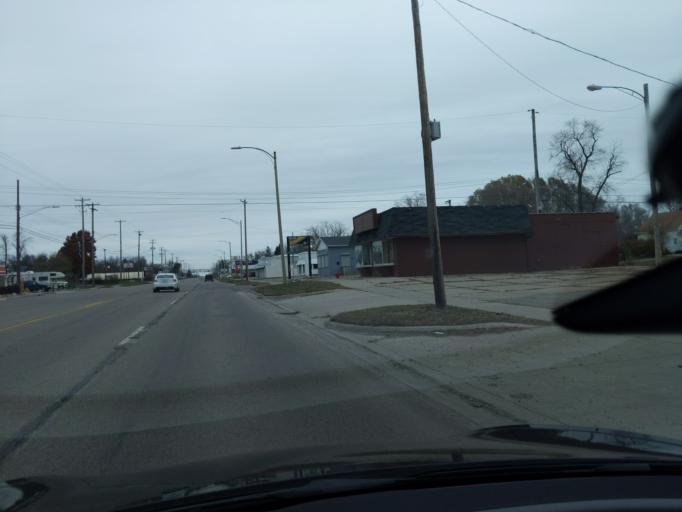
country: US
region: Michigan
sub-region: Ingham County
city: Lansing
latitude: 42.7652
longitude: -84.5427
